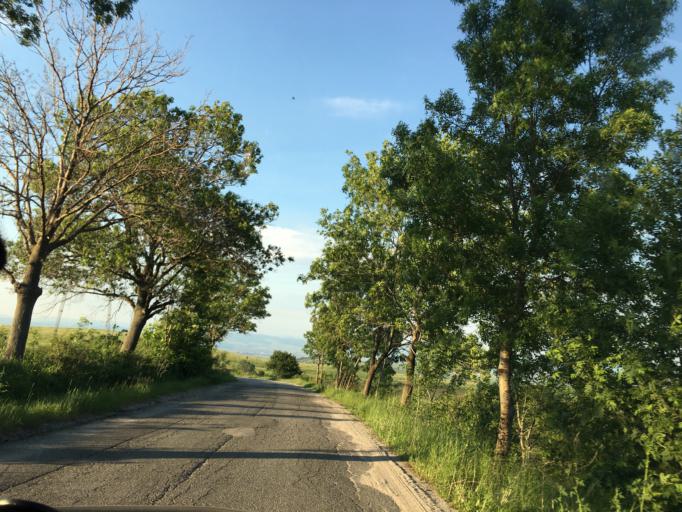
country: BG
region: Sofiya
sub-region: Obshtina Bozhurishte
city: Bozhurishte
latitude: 42.7239
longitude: 23.1034
